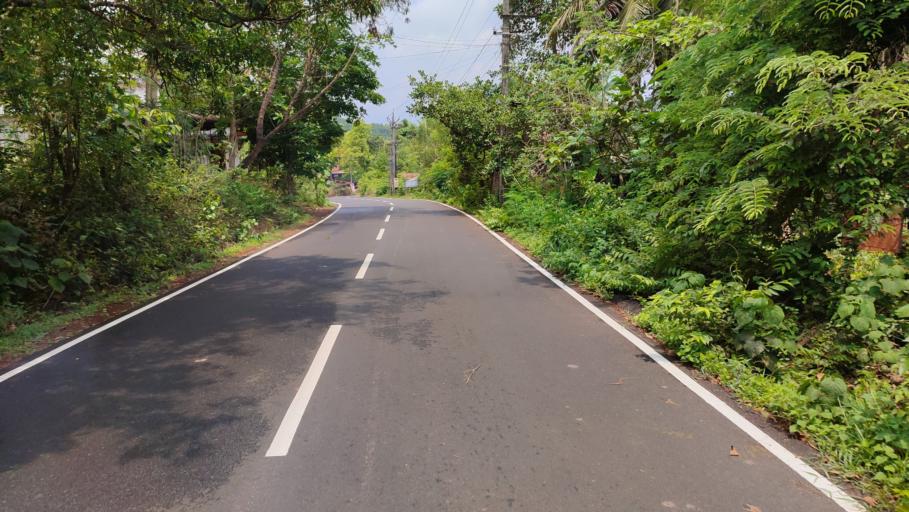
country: IN
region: Kerala
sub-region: Kasaragod District
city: Kannangad
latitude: 12.3215
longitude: 75.1355
